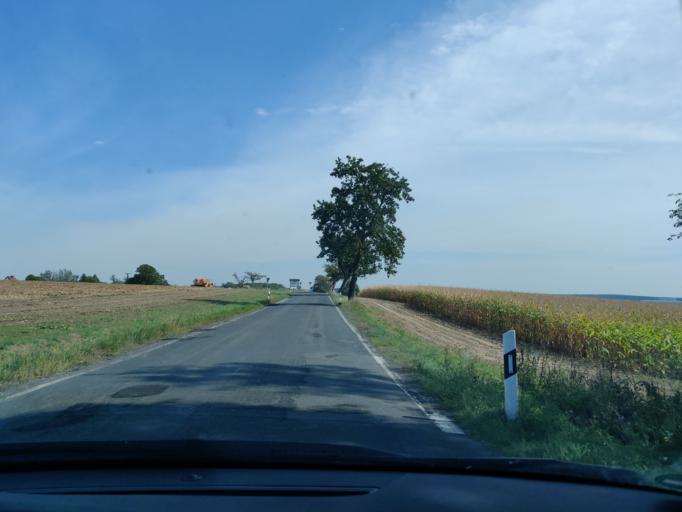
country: DE
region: Saxony
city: Kriebstein
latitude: 51.0356
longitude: 12.9835
